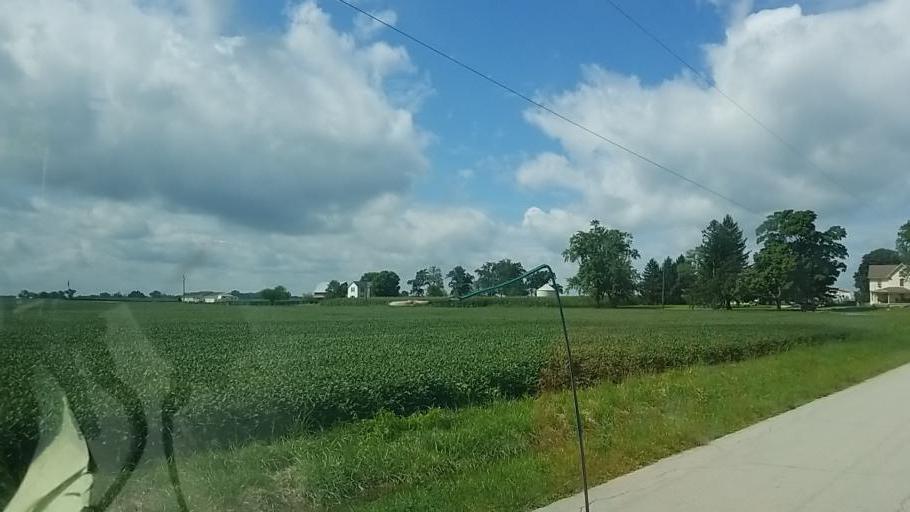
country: US
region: Ohio
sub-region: Fayette County
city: Jeffersonville
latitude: 39.6855
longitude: -83.5020
